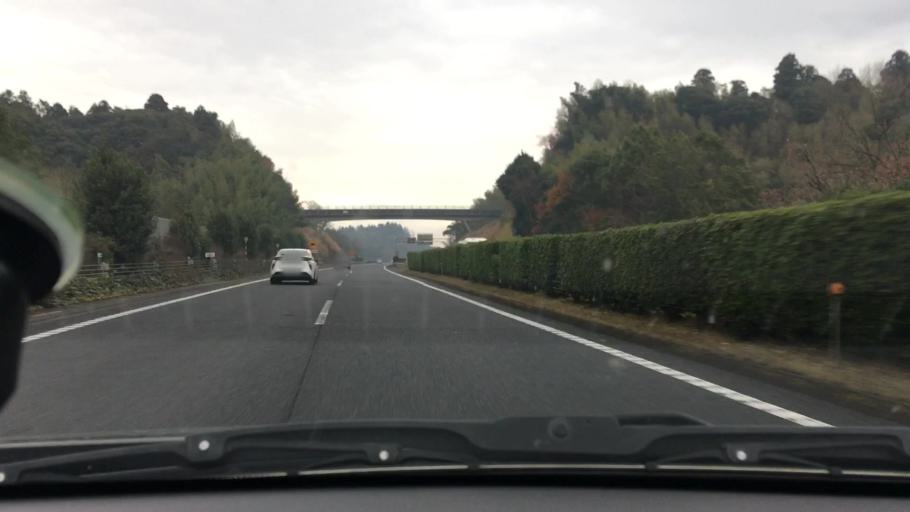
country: JP
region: Chiba
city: Narita
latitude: 35.7899
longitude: 140.3486
